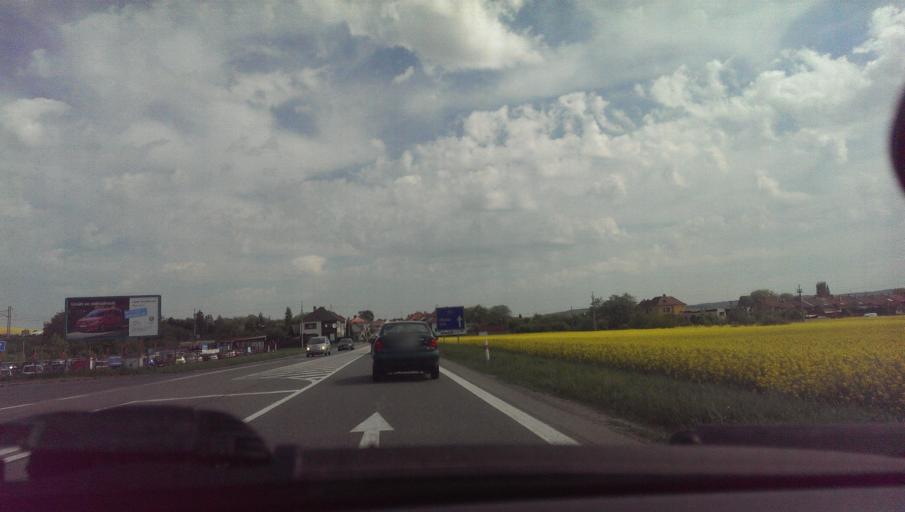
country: CZ
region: Zlin
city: Spytihnev
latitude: 49.1346
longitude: 17.4884
